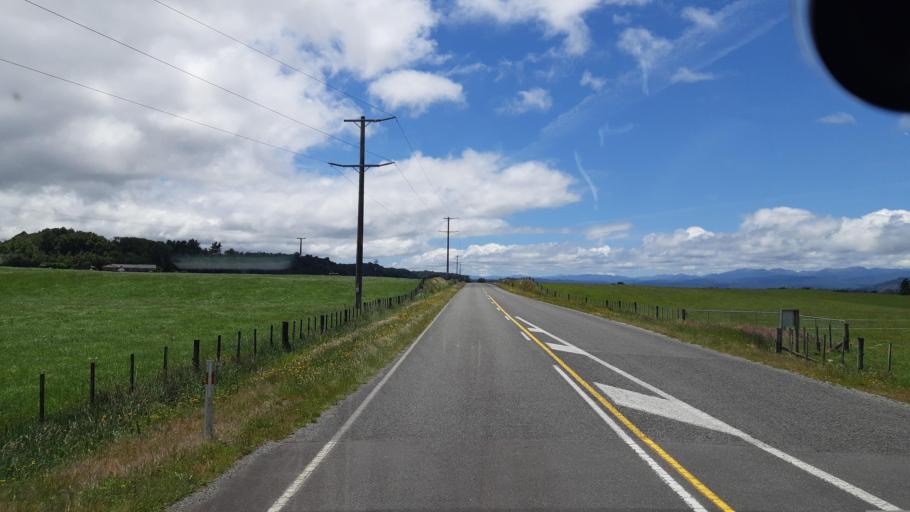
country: NZ
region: West Coast
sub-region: Grey District
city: Greymouth
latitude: -42.3166
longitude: 171.5421
